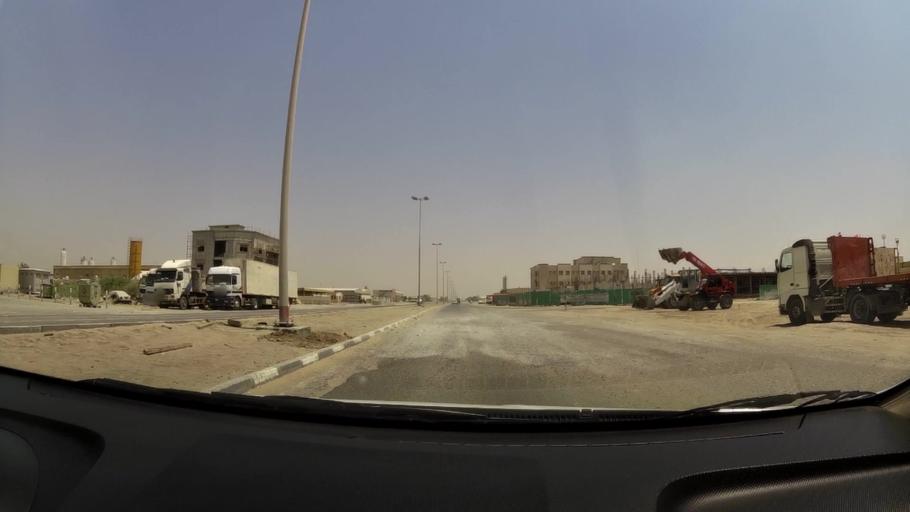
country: AE
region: Umm al Qaywayn
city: Umm al Qaywayn
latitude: 25.5106
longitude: 55.5583
